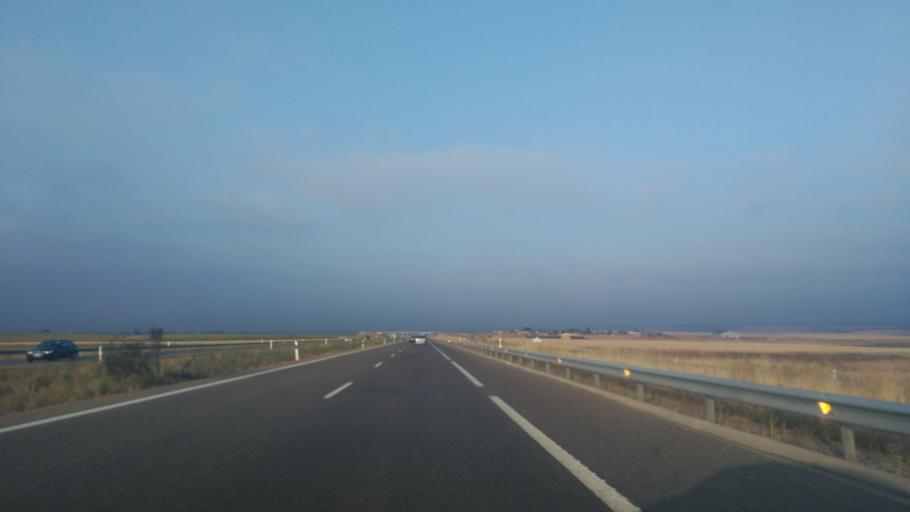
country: ES
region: Castille and Leon
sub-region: Provincia de Salamanca
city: Robliza de Cojos
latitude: 40.8854
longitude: -5.9562
